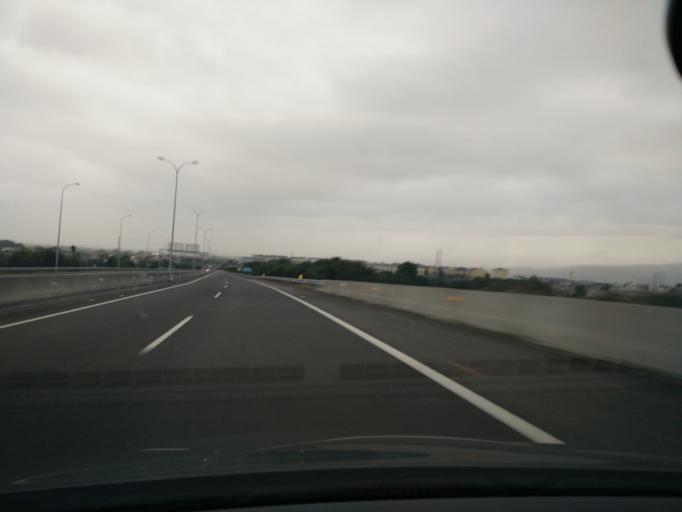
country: ES
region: Galicia
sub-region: Provincia de Lugo
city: Ribadeo
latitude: 43.5416
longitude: -7.0608
